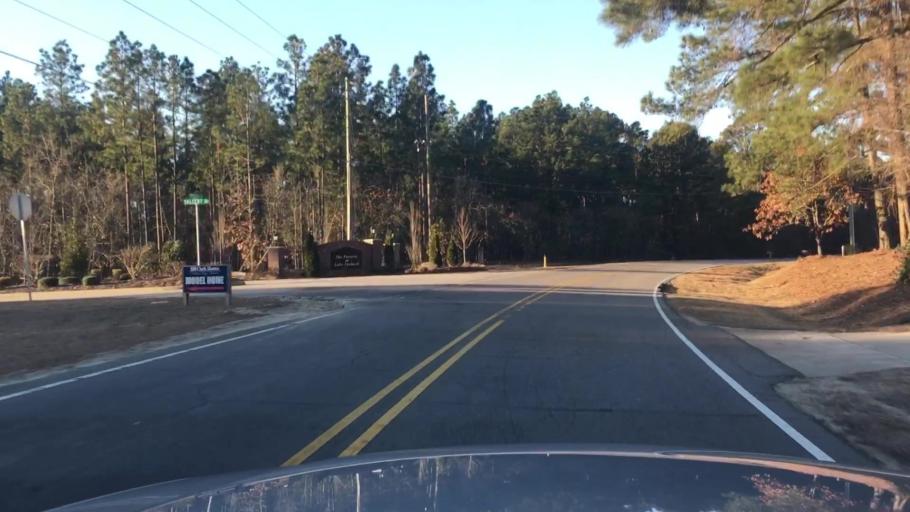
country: US
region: North Carolina
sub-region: Cumberland County
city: Hope Mills
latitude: 34.9640
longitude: -79.0087
